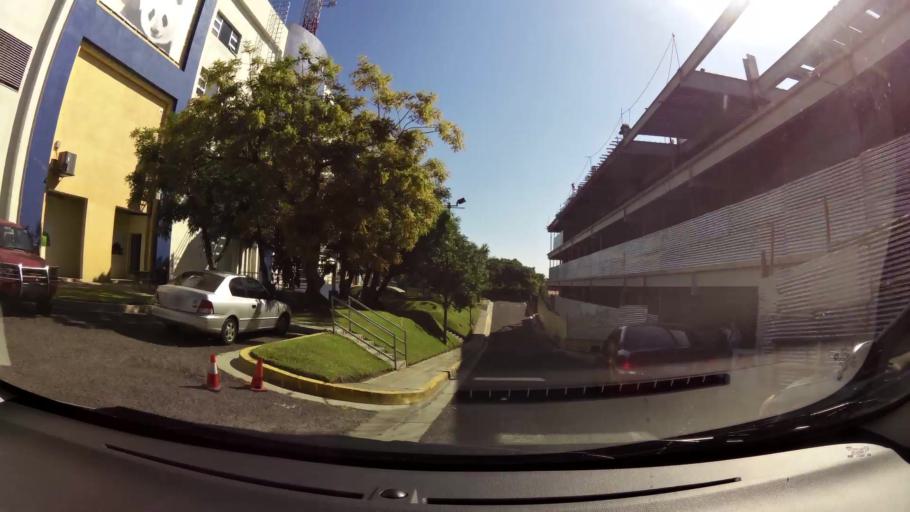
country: SV
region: La Libertad
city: Santa Tecla
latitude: 13.6776
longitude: -89.2767
